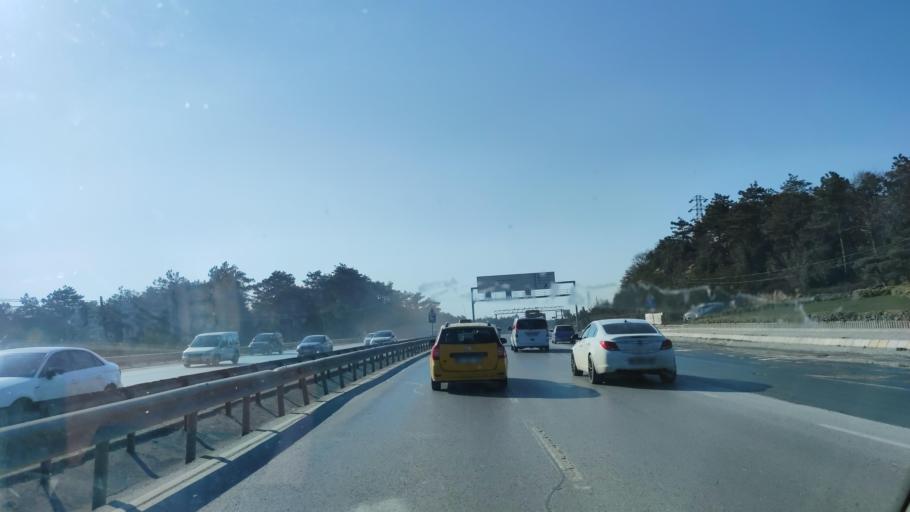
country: TR
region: Istanbul
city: Basaksehir
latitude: 41.1611
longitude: 28.7762
